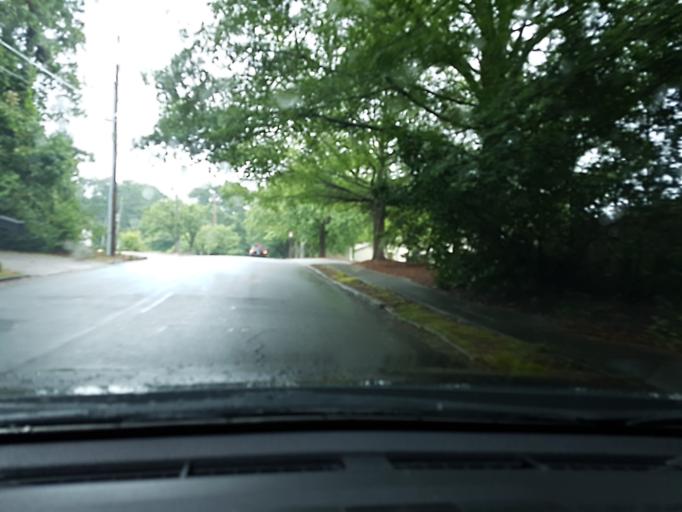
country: US
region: Georgia
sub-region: DeKalb County
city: North Atlanta
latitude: 33.8612
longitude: -84.3821
